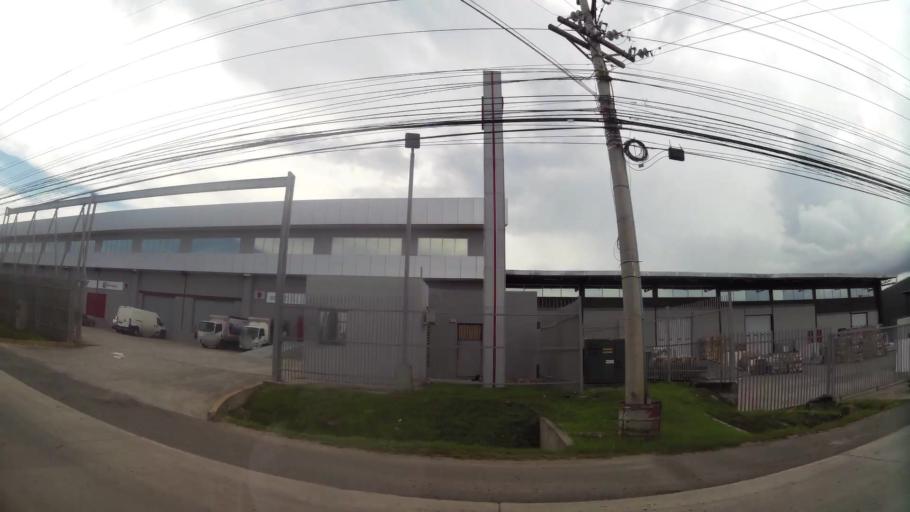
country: PA
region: Panama
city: Tocumen
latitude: 9.0768
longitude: -79.4014
